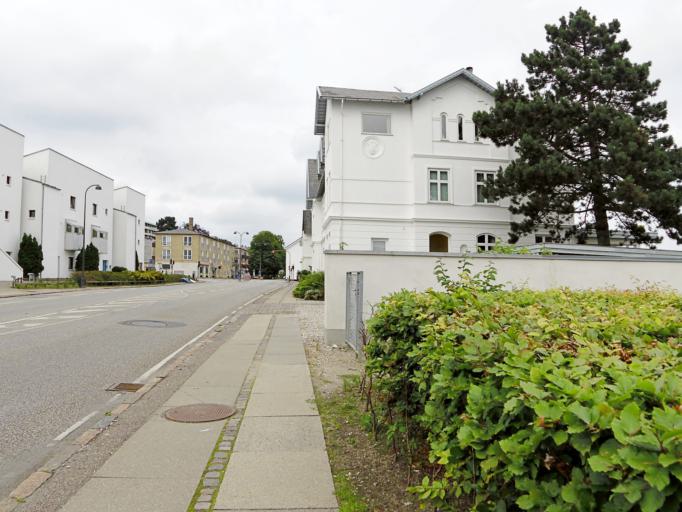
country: DK
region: Capital Region
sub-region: Rudersdal Kommune
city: Trorod
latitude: 55.8200
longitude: 12.5749
